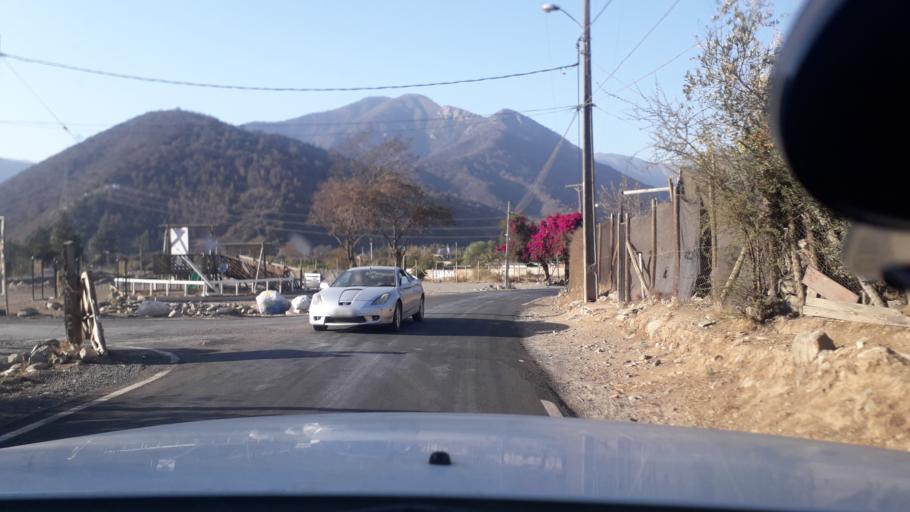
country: CL
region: Valparaiso
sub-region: Provincia de Marga Marga
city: Limache
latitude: -33.0541
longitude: -71.1118
